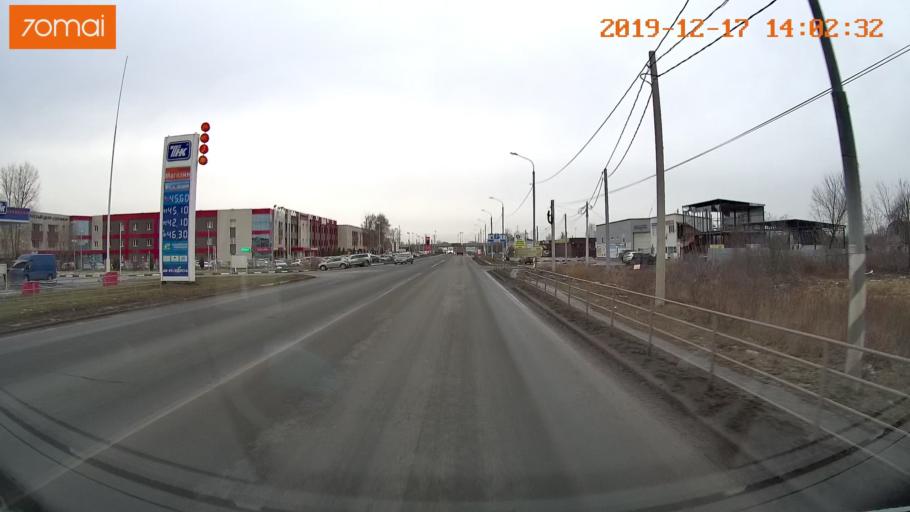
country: RU
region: Rjazan
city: Ryazan'
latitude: 54.6138
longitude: 39.6466
